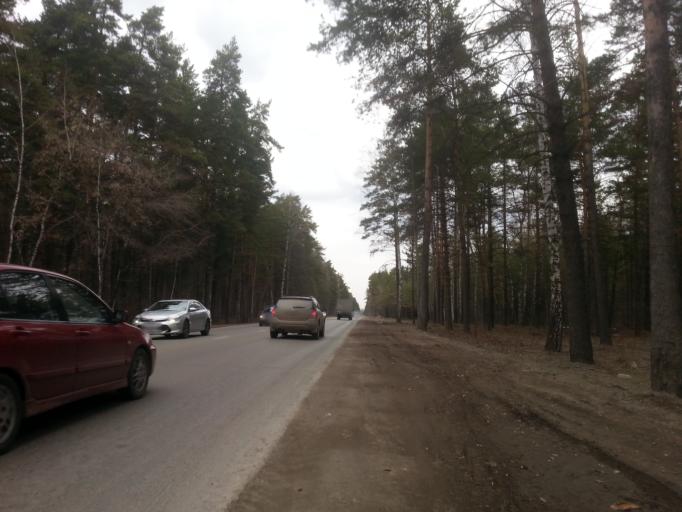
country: RU
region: Altai Krai
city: Yuzhnyy
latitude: 53.2728
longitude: 83.7230
